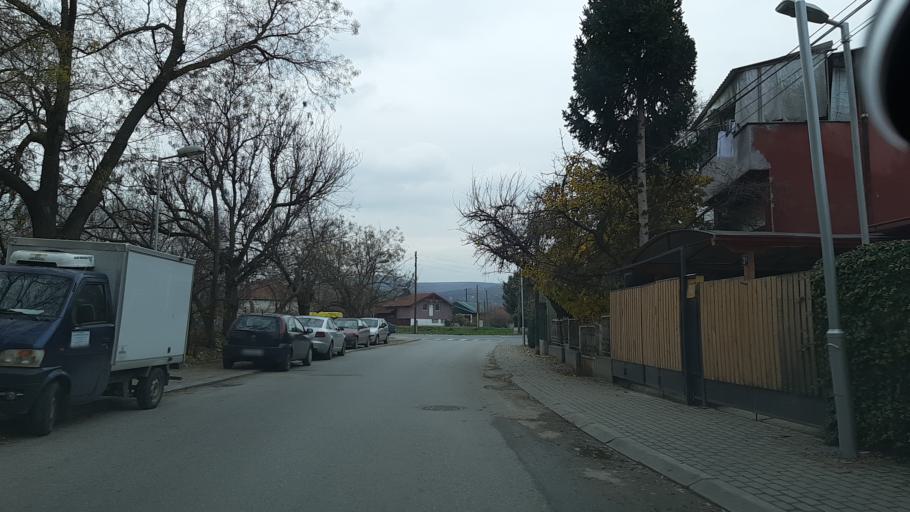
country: MK
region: Kisela Voda
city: Usje
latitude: 41.9718
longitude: 21.4778
